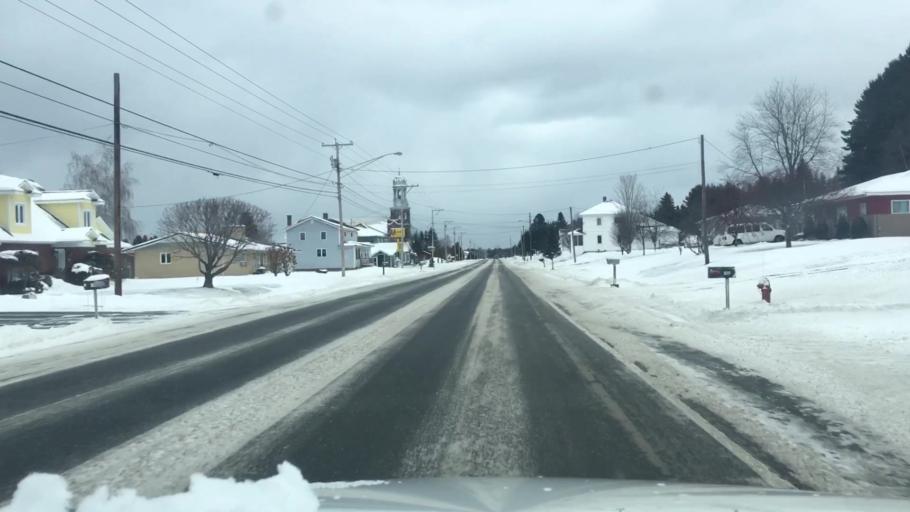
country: US
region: Maine
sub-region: Aroostook County
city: Madawaska
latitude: 47.3495
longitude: -68.2812
